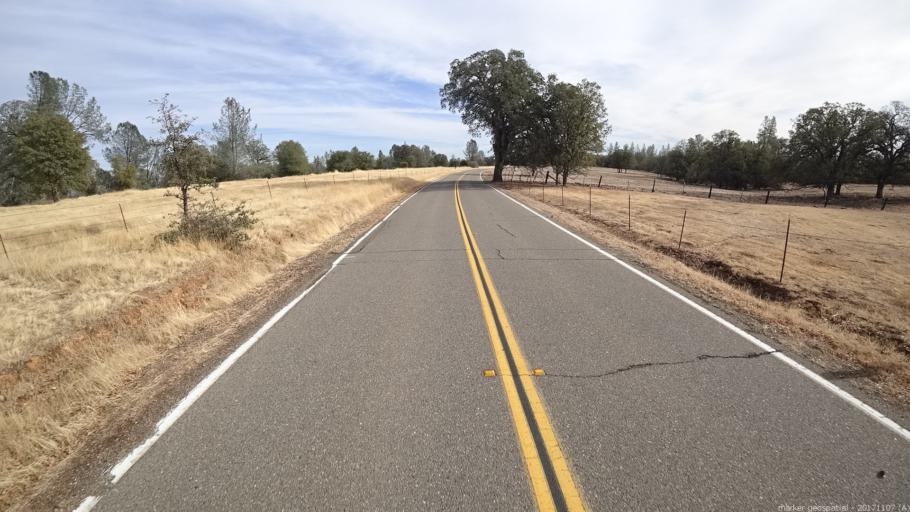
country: US
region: California
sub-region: Shasta County
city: Shasta
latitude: 40.5061
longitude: -122.5355
